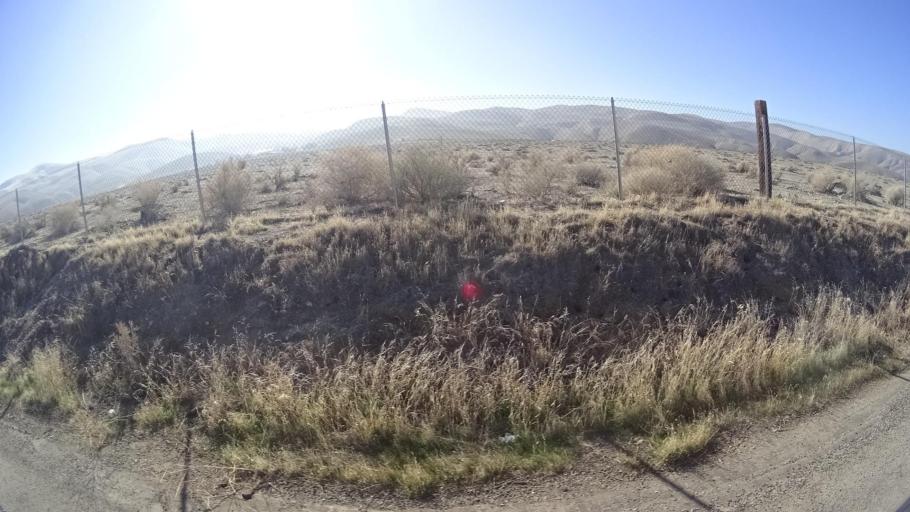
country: US
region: California
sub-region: Kern County
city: Maricopa
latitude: 34.9937
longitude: -119.3933
